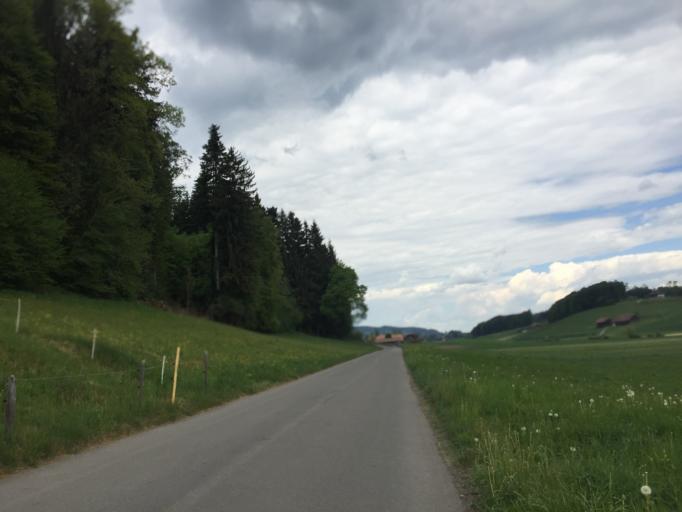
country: CH
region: Bern
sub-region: Thun District
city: Seftigen
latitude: 46.7930
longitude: 7.5570
